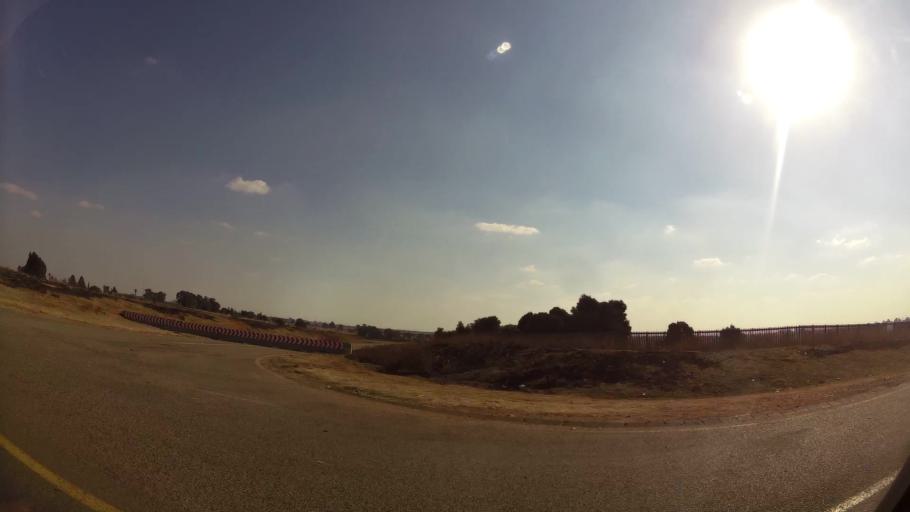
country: ZA
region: Gauteng
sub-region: Ekurhuleni Metropolitan Municipality
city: Benoni
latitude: -26.2357
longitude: 28.3219
